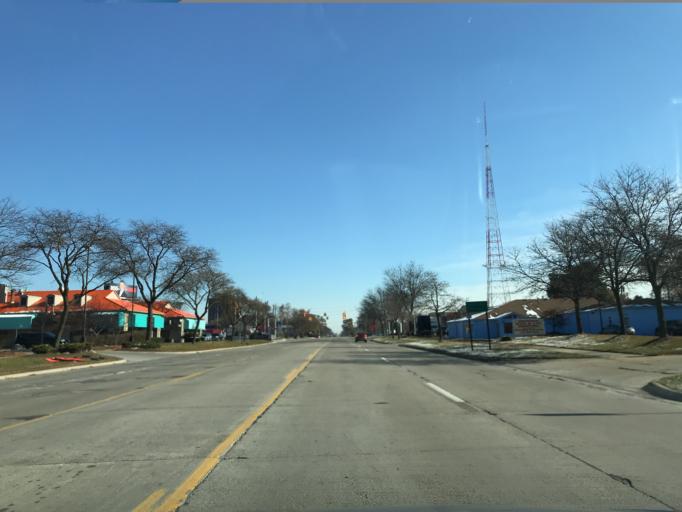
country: US
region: Michigan
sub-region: Oakland County
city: Southfield
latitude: 42.4738
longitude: -83.2041
